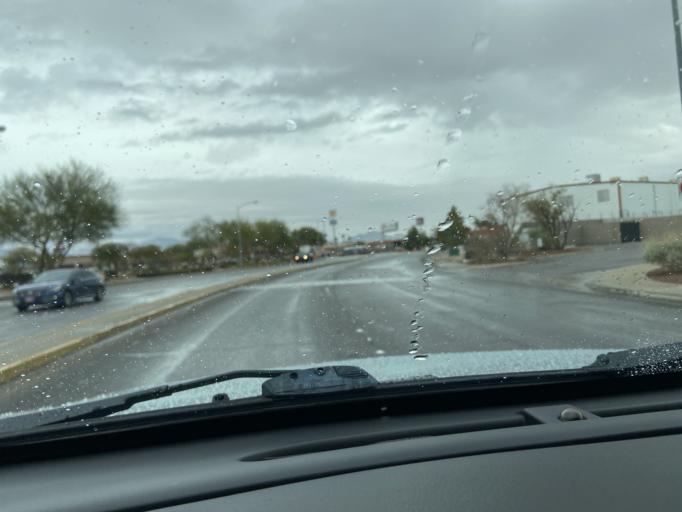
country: US
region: Nevada
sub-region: Clark County
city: Sunrise Manor
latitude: 36.2378
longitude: -115.0985
